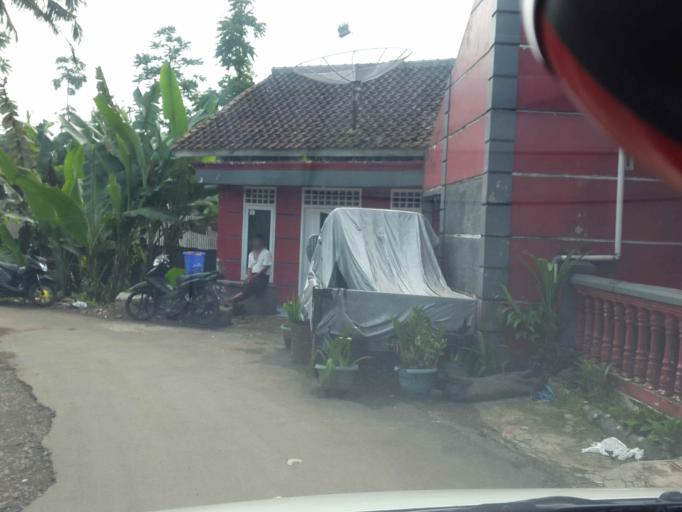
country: ID
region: West Java
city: Sukabumi
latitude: -6.8993
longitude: 106.9617
